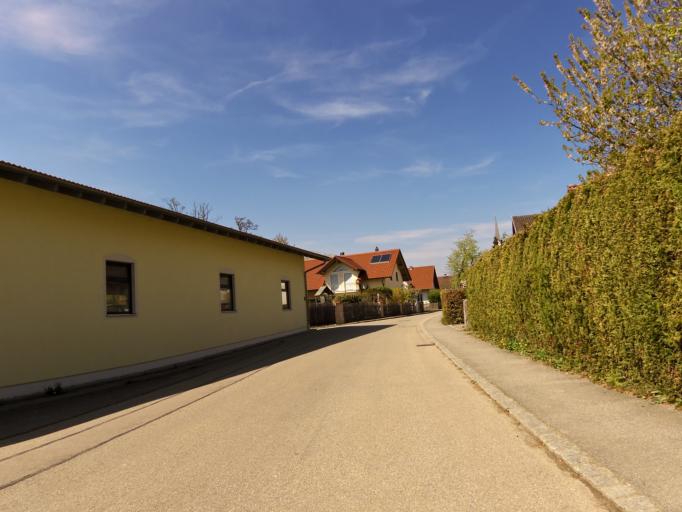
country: DE
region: Bavaria
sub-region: Upper Bavaria
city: Fraunberg
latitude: 48.3660
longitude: 11.9930
